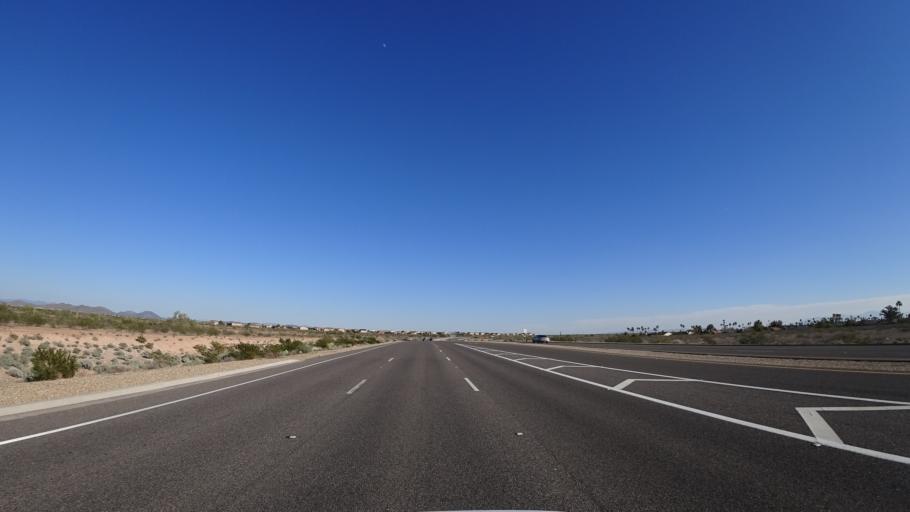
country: US
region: Arizona
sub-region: Maricopa County
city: Sun City West
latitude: 33.6846
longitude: -112.3287
